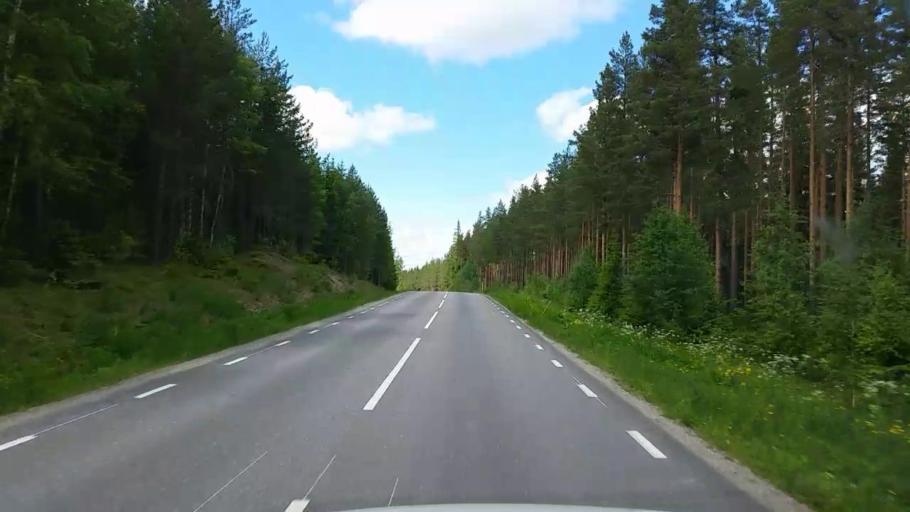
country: SE
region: Gaevleborg
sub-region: Ovanakers Kommun
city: Alfta
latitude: 61.2789
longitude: 16.1042
